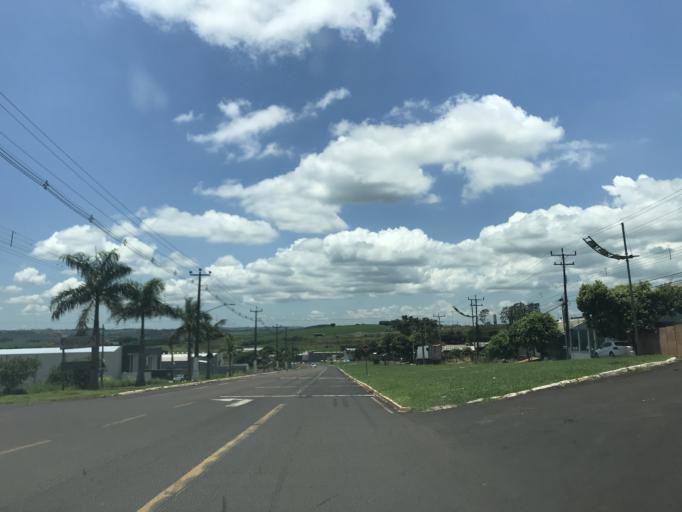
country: BR
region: Parana
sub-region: Marialva
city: Marialva
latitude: -23.4953
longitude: -51.7801
